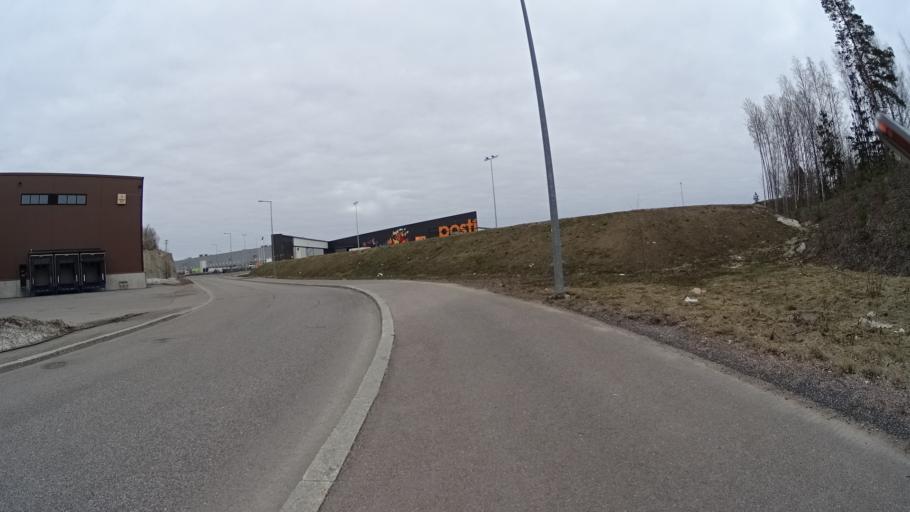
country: FI
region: Uusimaa
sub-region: Helsinki
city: Teekkarikylae
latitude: 60.3020
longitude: 24.8953
